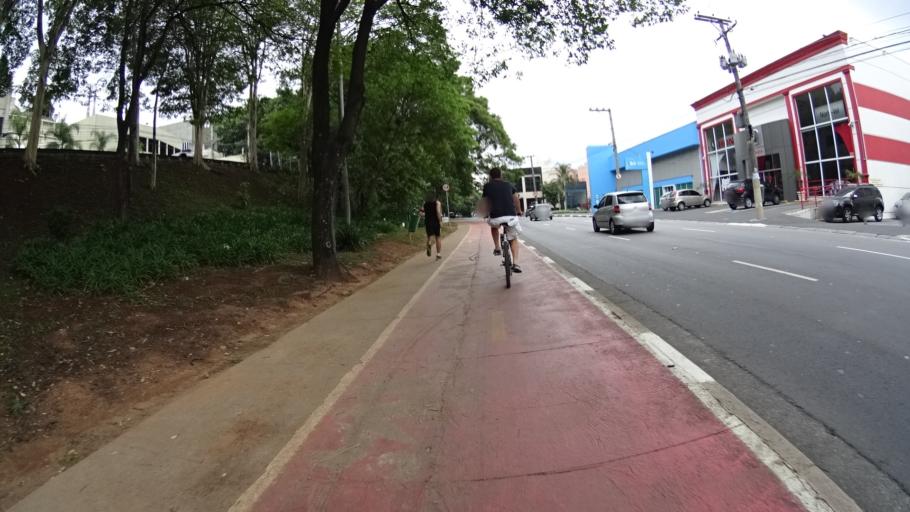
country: BR
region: Sao Paulo
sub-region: Sao Paulo
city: Sao Paulo
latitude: -23.5059
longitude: -46.6427
